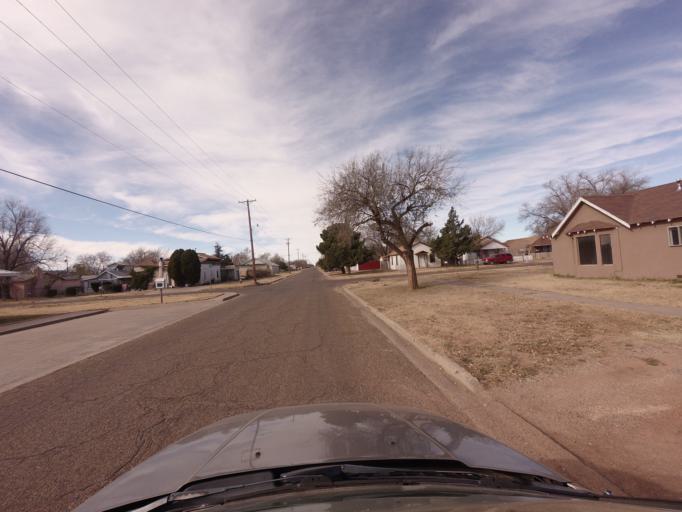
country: US
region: New Mexico
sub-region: Curry County
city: Clovis
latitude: 34.4089
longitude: -103.1974
